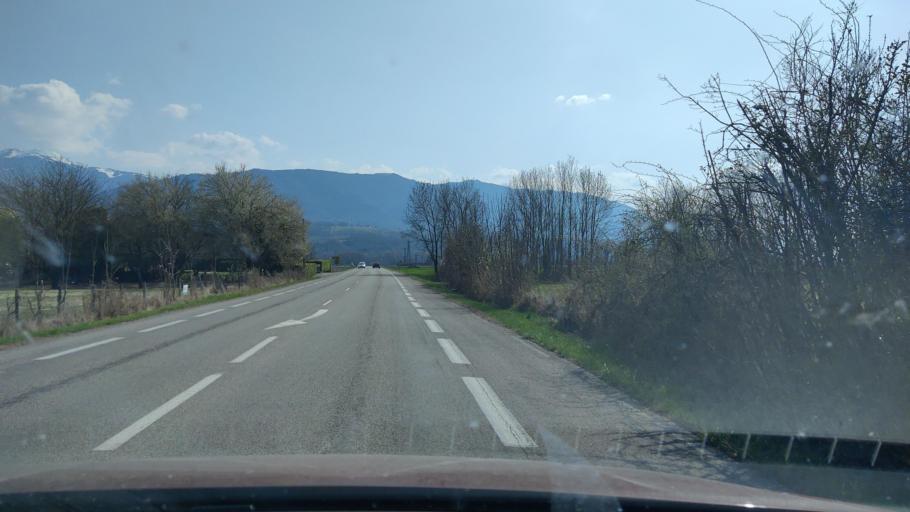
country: FR
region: Rhone-Alpes
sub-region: Departement de la Savoie
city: Montmelian
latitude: 45.4759
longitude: 6.0416
